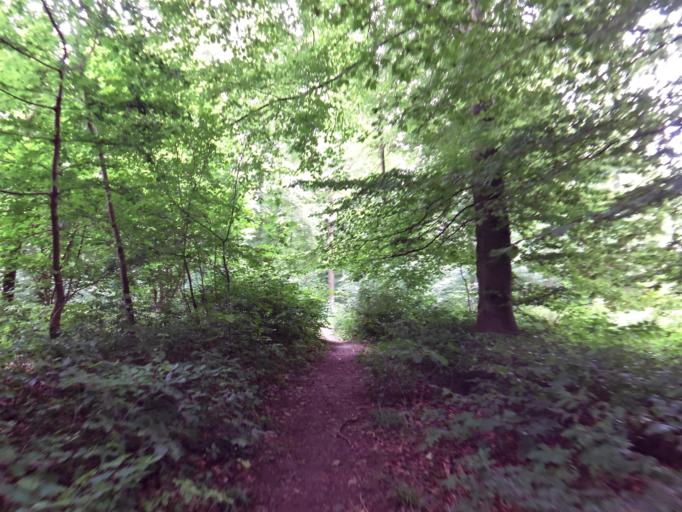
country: CH
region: Zurich
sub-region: Bezirk Zuerich
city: Zuerich (Kreis 5) / Escher-Wyss
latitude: 47.4024
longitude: 8.5151
